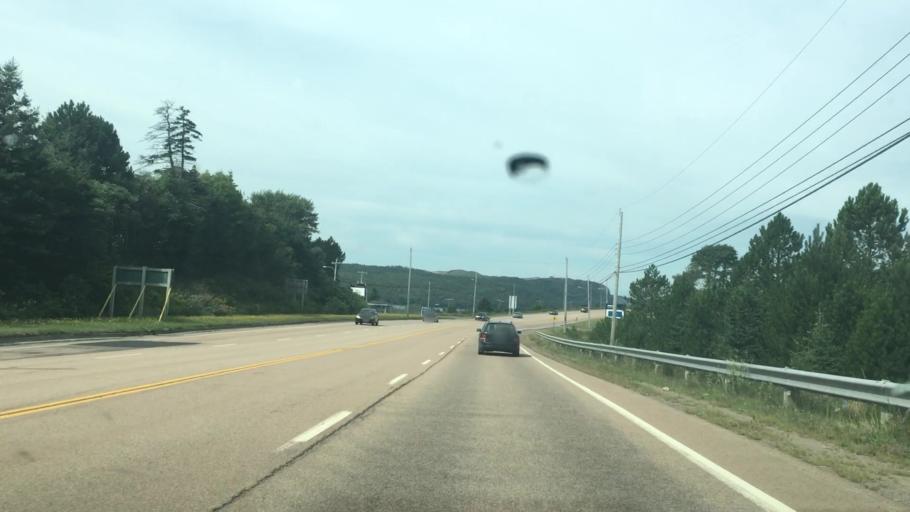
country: CA
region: Nova Scotia
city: Port Hawkesbury
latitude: 45.6252
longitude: -61.3675
